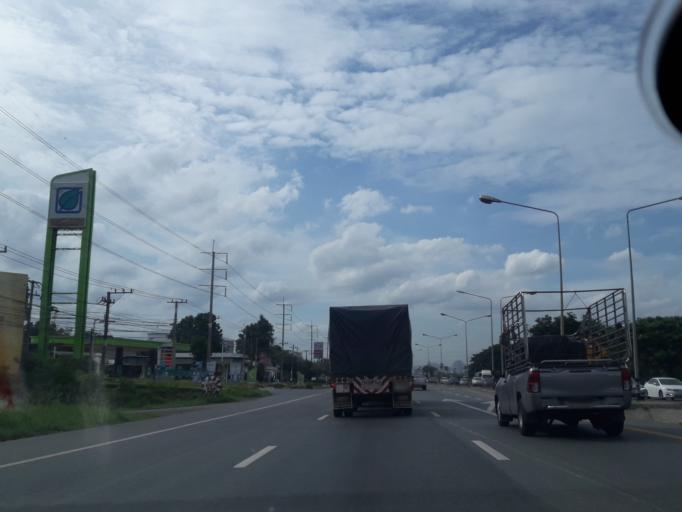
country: TH
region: Sara Buri
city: Chaloem Phra Kiat
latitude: 14.5959
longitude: 100.8968
